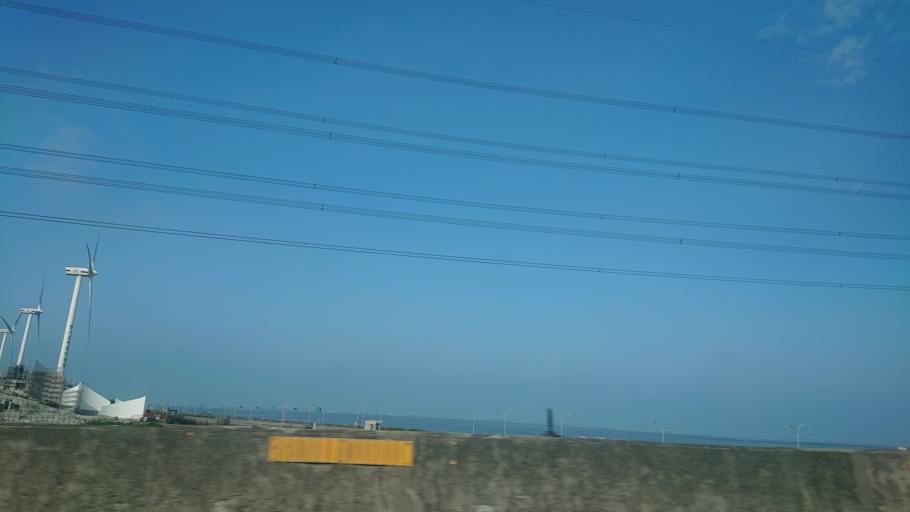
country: TW
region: Taiwan
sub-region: Changhua
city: Chang-hua
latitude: 24.1577
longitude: 120.4593
